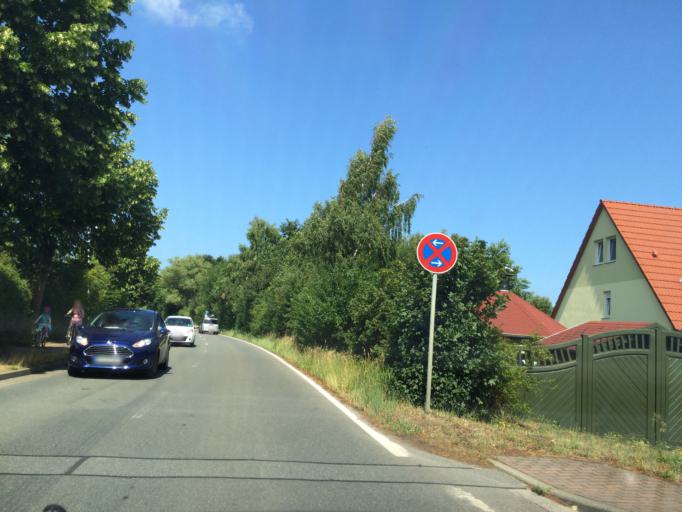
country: DE
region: Mecklenburg-Vorpommern
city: Zingst
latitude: 54.4371
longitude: 12.6744
